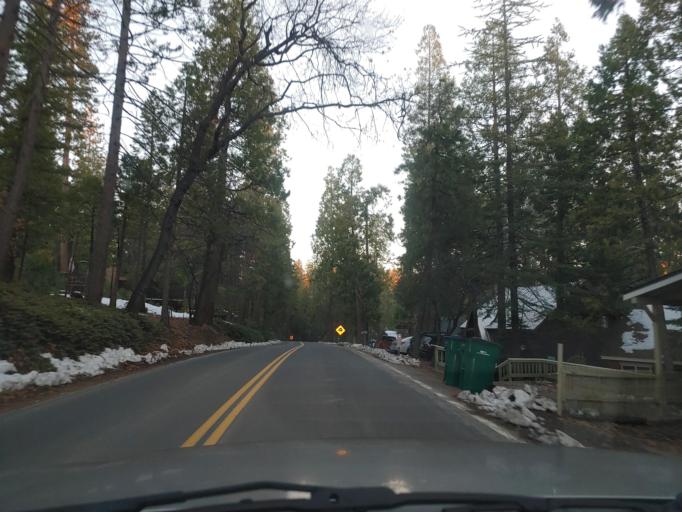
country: US
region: California
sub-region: Tuolumne County
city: Twain Harte
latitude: 38.0389
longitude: -120.2361
